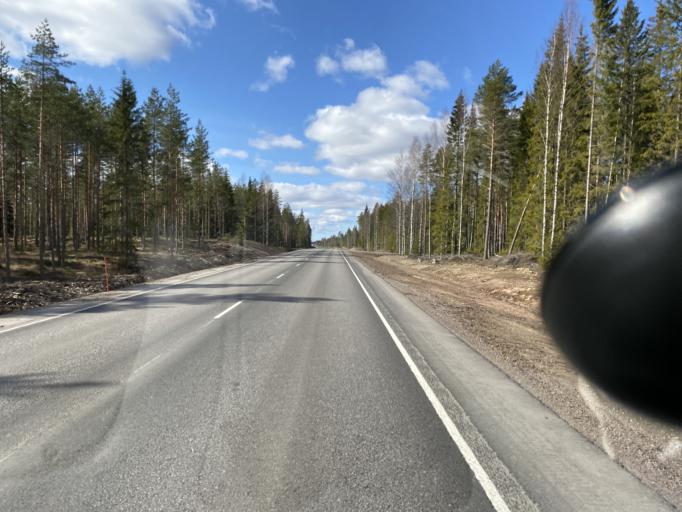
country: FI
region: Satakunta
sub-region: Pori
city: Huittinen
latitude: 61.1735
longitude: 22.5275
